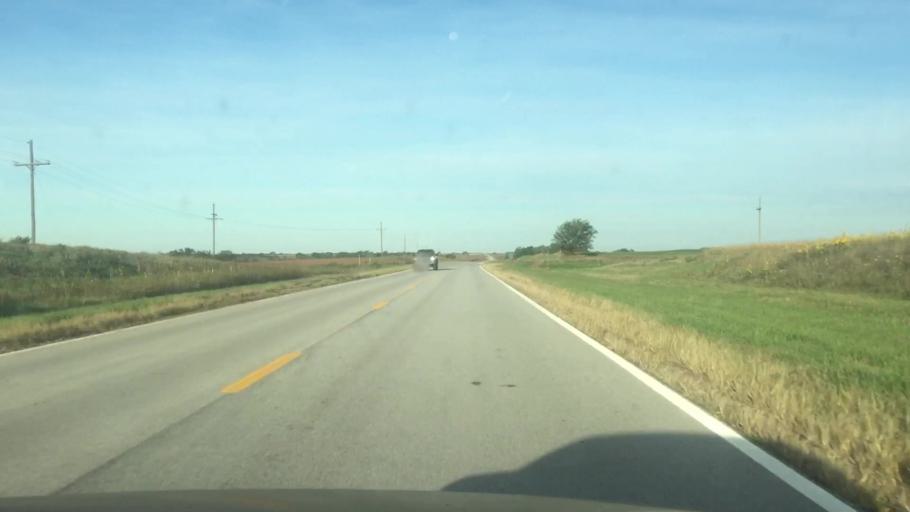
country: US
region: Nebraska
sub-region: Gage County
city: Wymore
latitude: 40.0447
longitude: -96.6694
